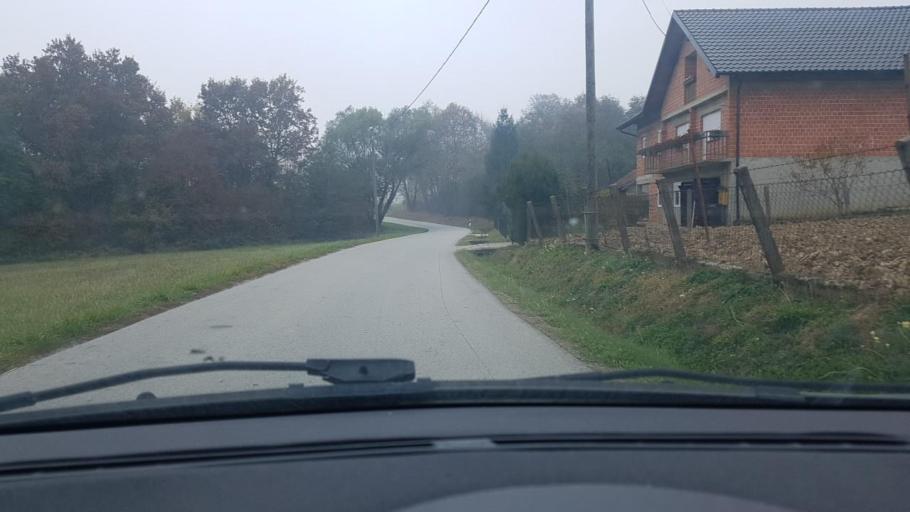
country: HR
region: Krapinsko-Zagorska
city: Marija Bistrica
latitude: 46.0644
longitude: 16.1741
